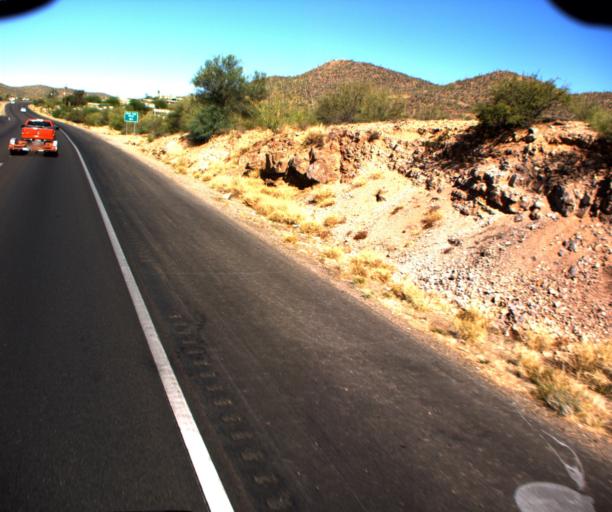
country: US
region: Arizona
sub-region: Pima County
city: Drexel Heights
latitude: 32.1777
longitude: -111.0153
